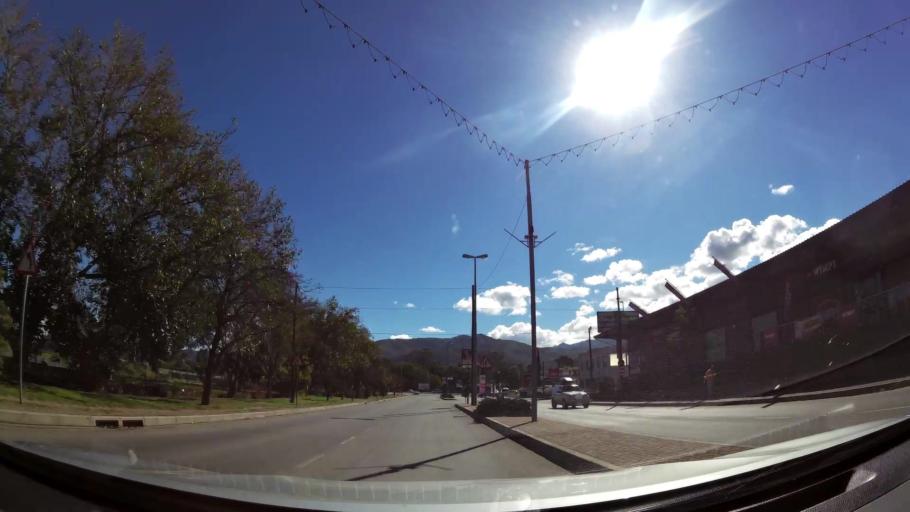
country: ZA
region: Western Cape
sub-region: Cape Winelands District Municipality
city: Ashton
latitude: -33.8066
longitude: 19.8765
